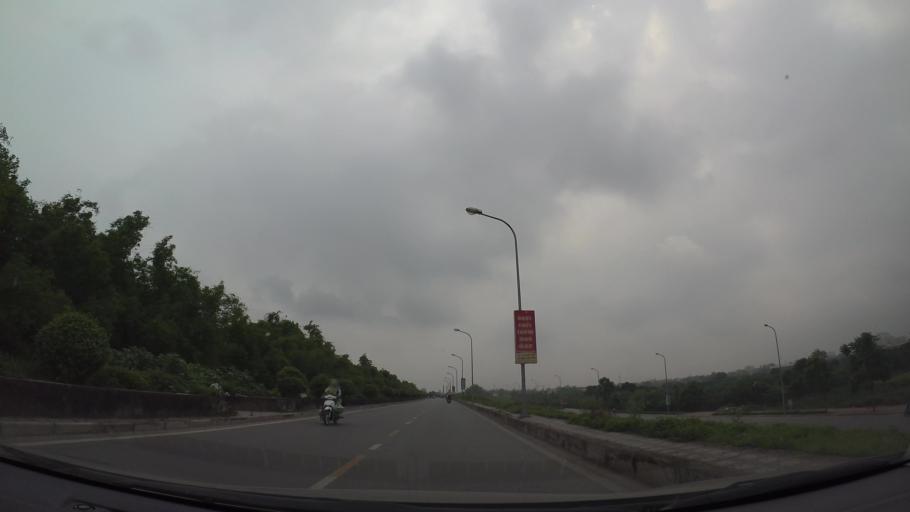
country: VN
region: Ha Noi
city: Hoan Kiem
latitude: 21.0755
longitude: 105.8931
